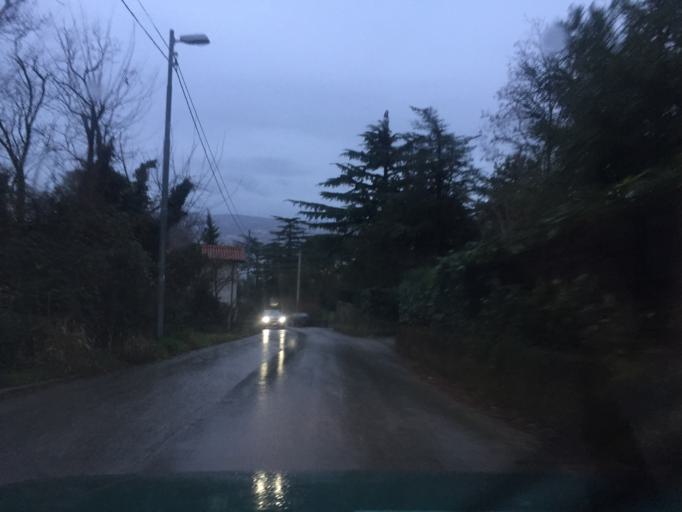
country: IT
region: Friuli Venezia Giulia
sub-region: Provincia di Trieste
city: Muggia
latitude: 45.6017
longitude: 13.7563
